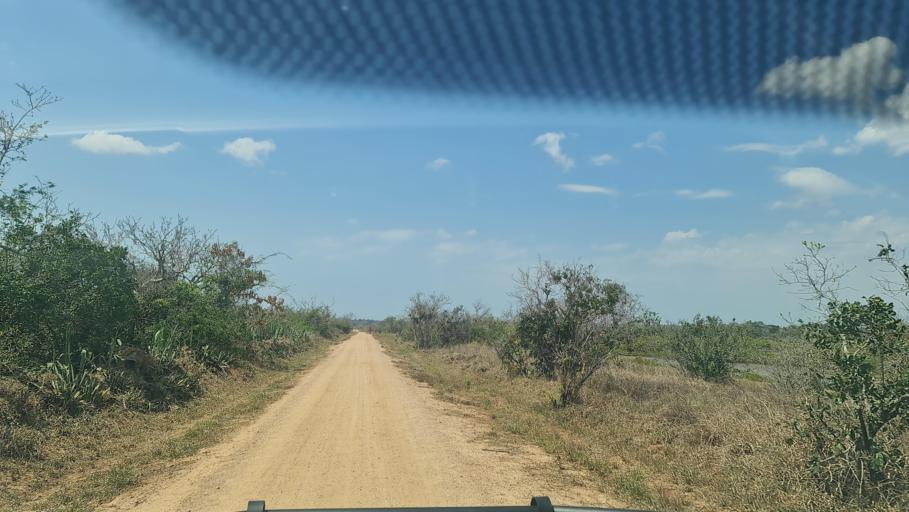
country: MZ
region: Nampula
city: Ilha de Mocambique
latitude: -15.1826
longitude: 40.5163
